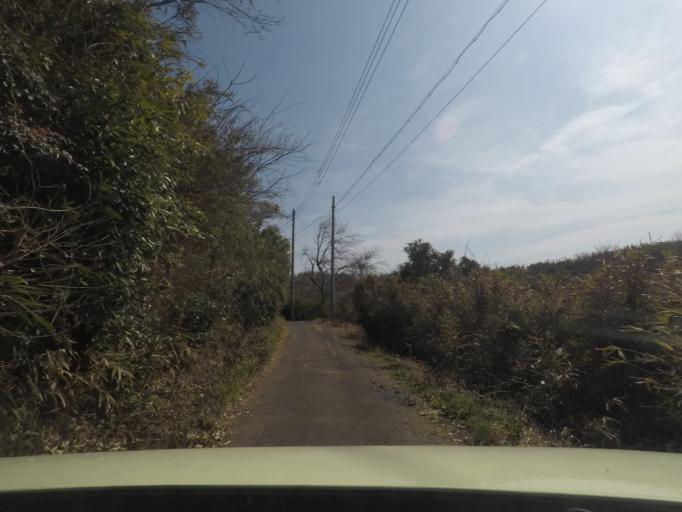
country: JP
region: Ibaraki
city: Ishioka
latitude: 36.1786
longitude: 140.3755
